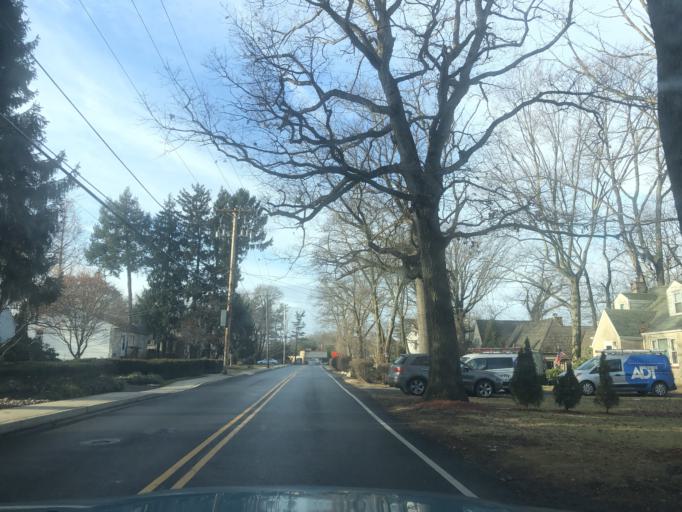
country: US
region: Pennsylvania
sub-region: Montgomery County
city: Jenkintown
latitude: 40.1187
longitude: -75.1339
